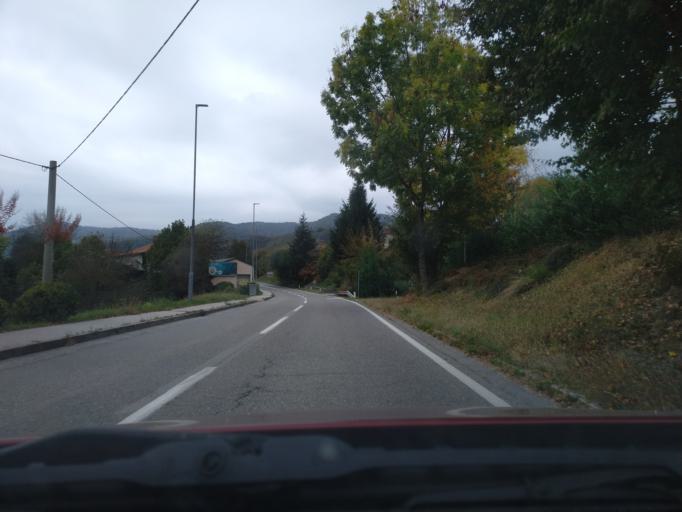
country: SI
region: Kanal
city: Kanal
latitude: 46.1084
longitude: 13.6740
